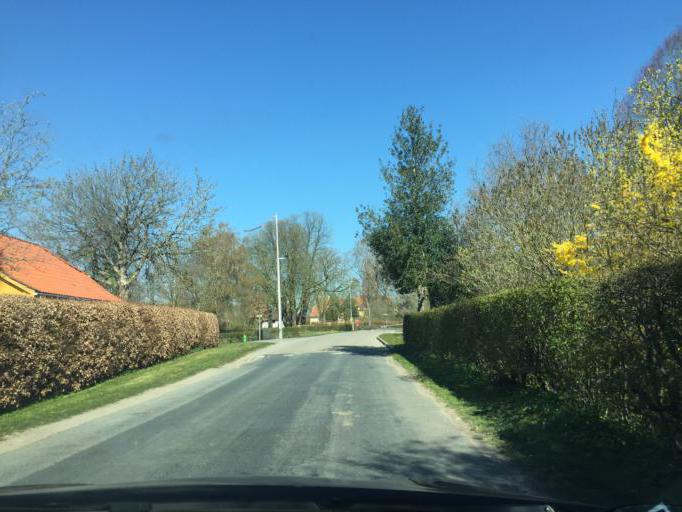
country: DK
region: South Denmark
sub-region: Faaborg-Midtfyn Kommune
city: Arslev
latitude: 55.2851
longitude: 10.5367
